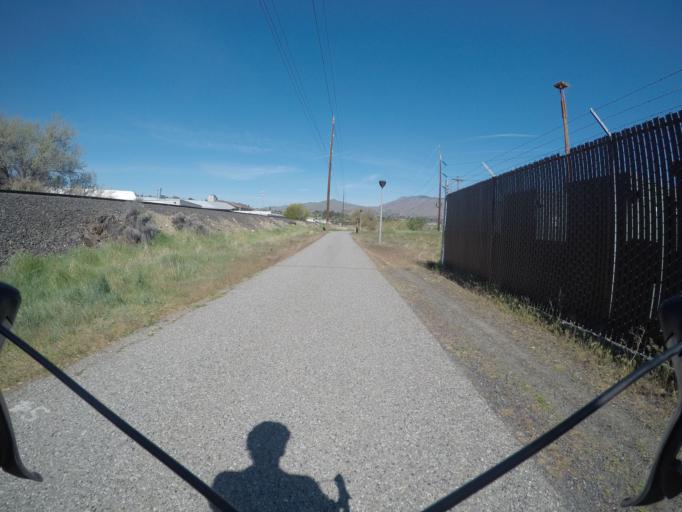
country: US
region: Washington
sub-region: Chelan County
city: Sunnyslope
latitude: 47.4516
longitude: -120.3305
